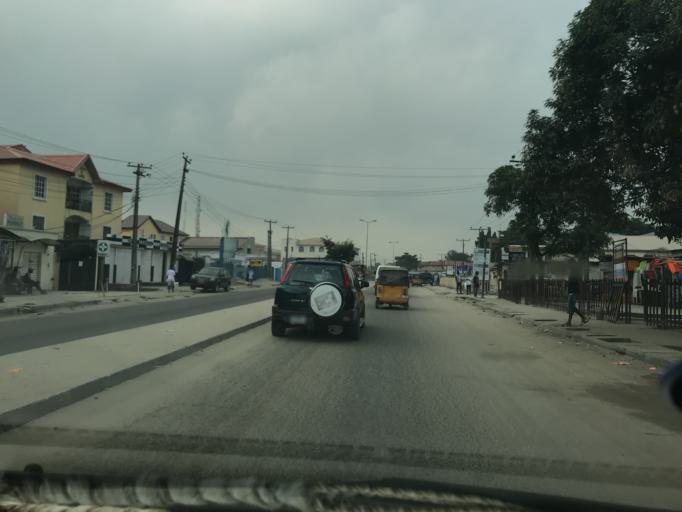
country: NG
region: Lagos
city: Ikoyi
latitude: 6.4737
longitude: 3.5670
